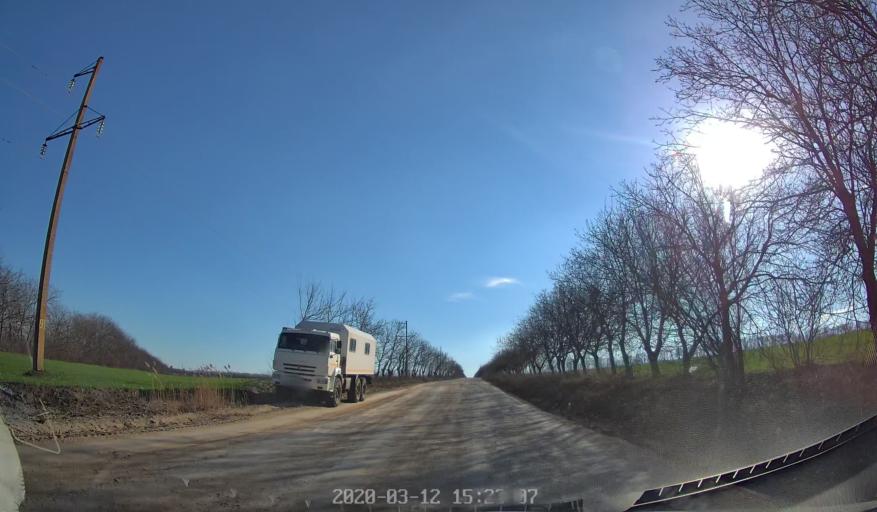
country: MD
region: Chisinau
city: Ciorescu
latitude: 47.1936
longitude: 28.9174
